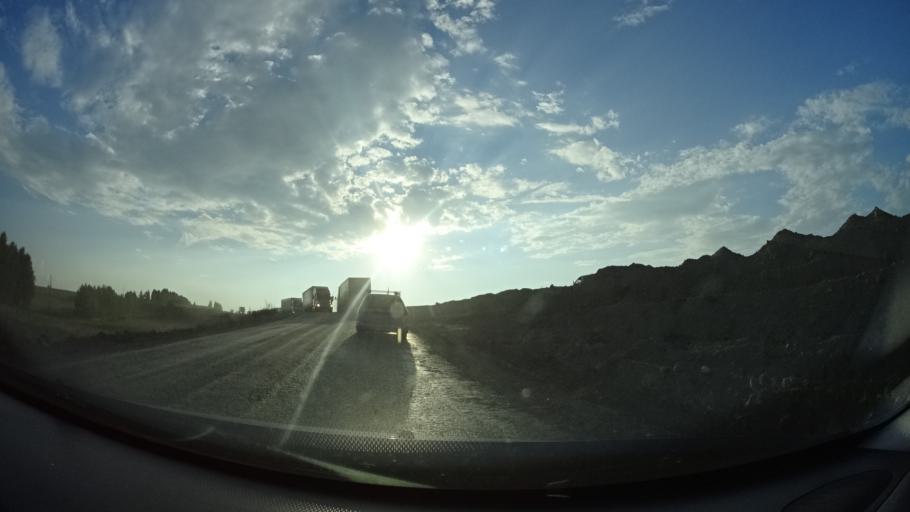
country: RU
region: Samara
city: Kamyshla
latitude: 54.0679
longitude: 52.1657
